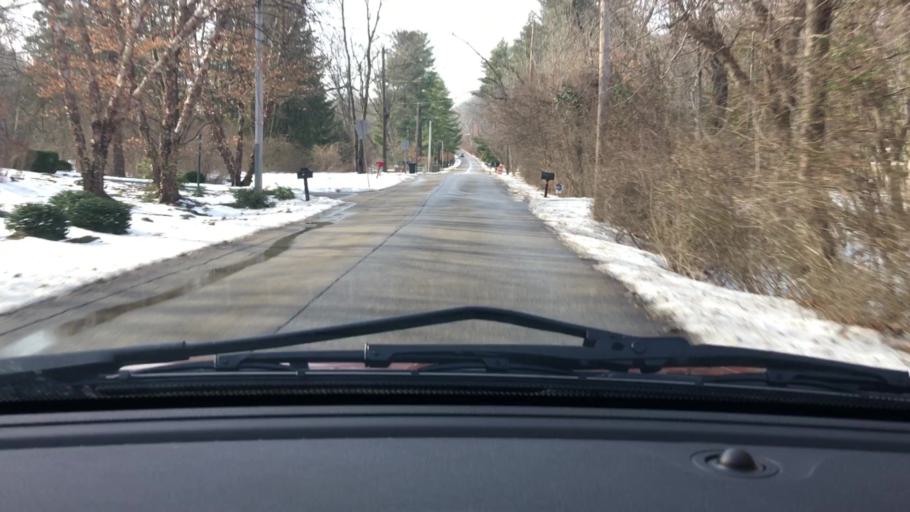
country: US
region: Pennsylvania
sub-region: Montgomery County
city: Flourtown
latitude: 40.0832
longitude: -75.2399
